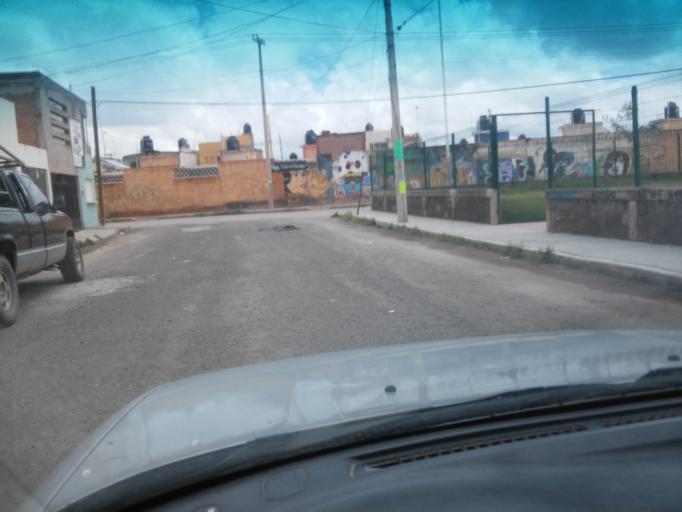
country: MX
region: Durango
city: Victoria de Durango
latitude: 24.0119
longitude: -104.6214
